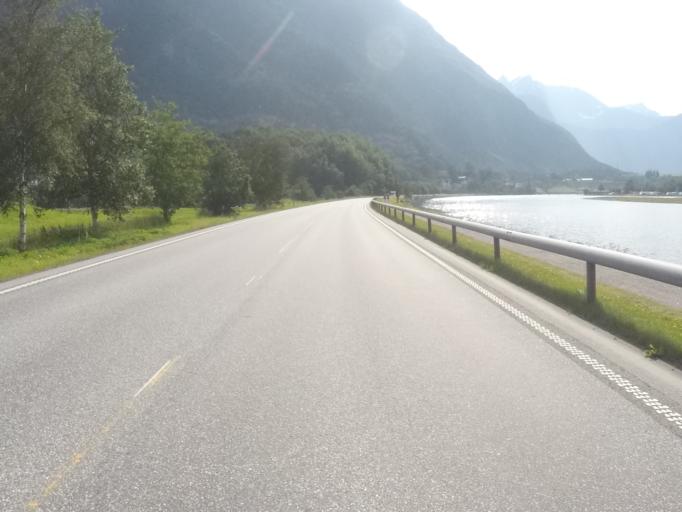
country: NO
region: More og Romsdal
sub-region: Rauma
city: Andalsnes
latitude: 62.5572
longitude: 7.6936
